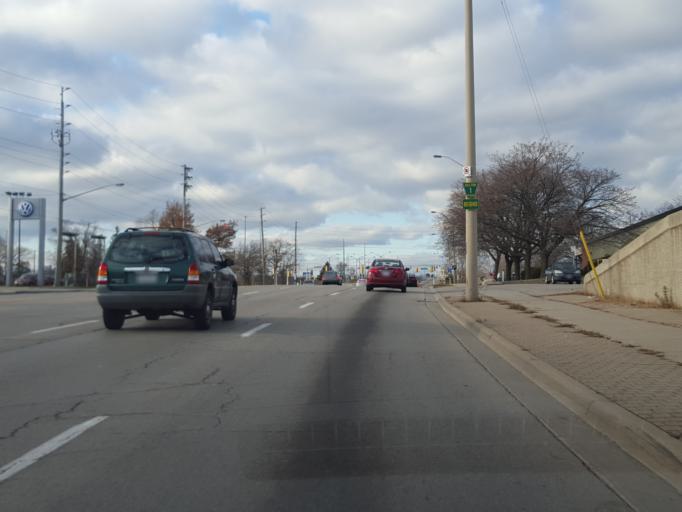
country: CA
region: Ontario
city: Burlington
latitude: 43.3488
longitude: -79.7994
